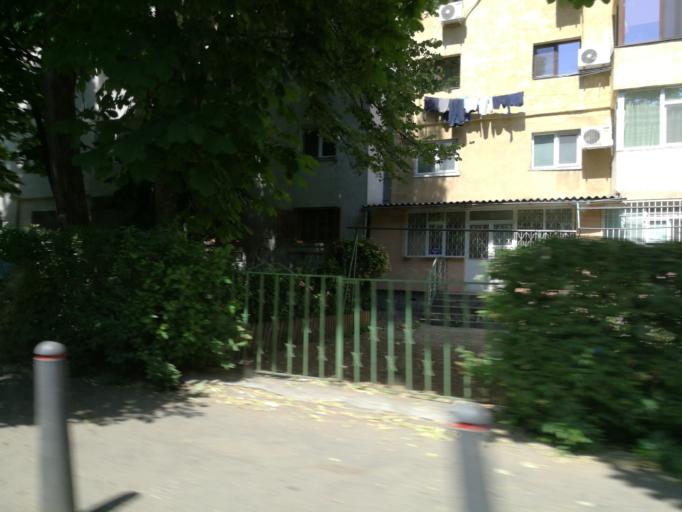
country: RO
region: Constanta
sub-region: Municipiul Constanta
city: Constanta
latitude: 44.2028
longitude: 28.6276
